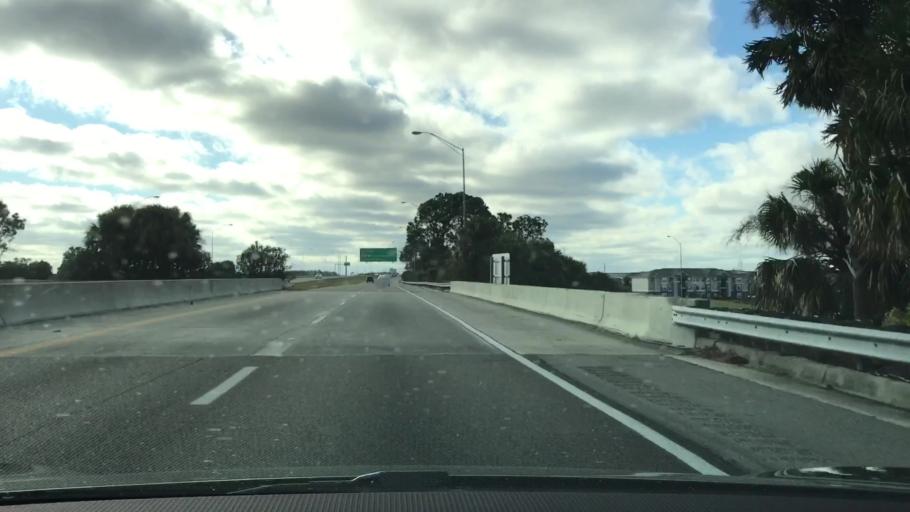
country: US
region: Florida
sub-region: Orange County
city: Meadow Woods
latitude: 28.3689
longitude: -81.3668
